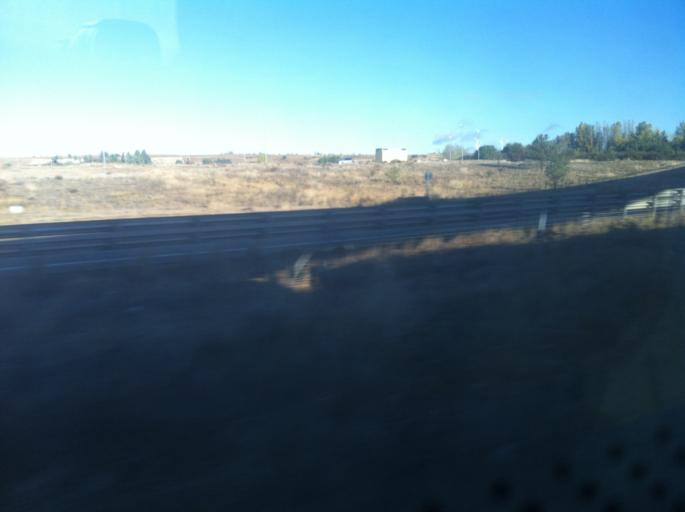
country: ES
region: Castille and Leon
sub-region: Provincia de Palencia
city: Venta de Banos
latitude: 41.9393
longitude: -4.4713
